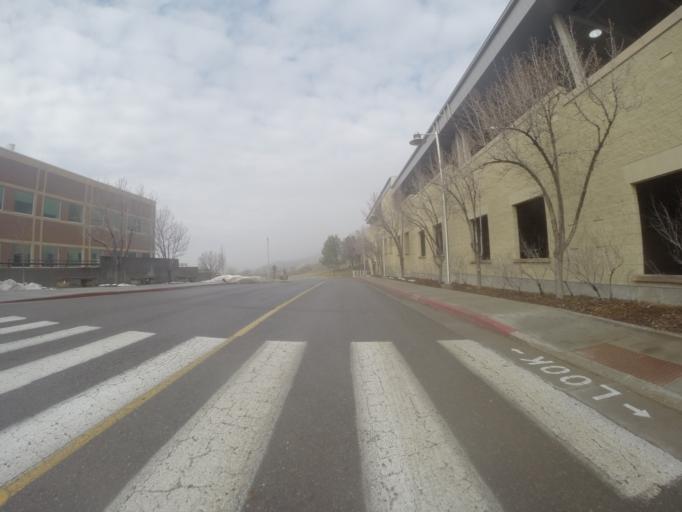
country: US
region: Utah
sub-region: Salt Lake County
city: Salt Lake City
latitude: 40.7726
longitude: -111.8357
